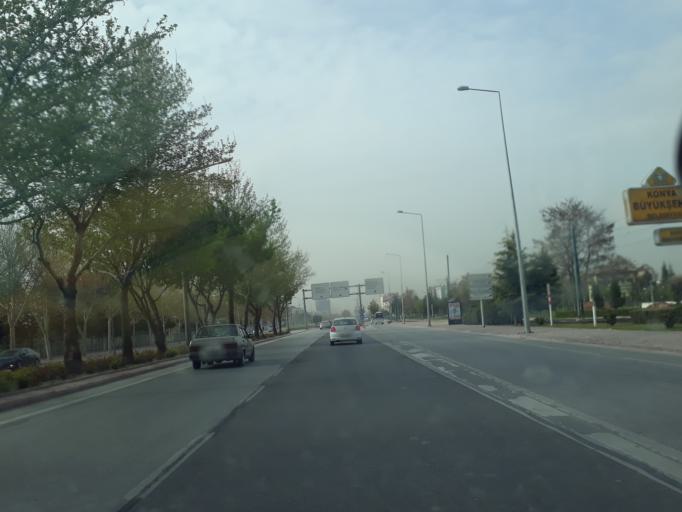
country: TR
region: Konya
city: Selcuklu
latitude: 37.9531
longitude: 32.5133
